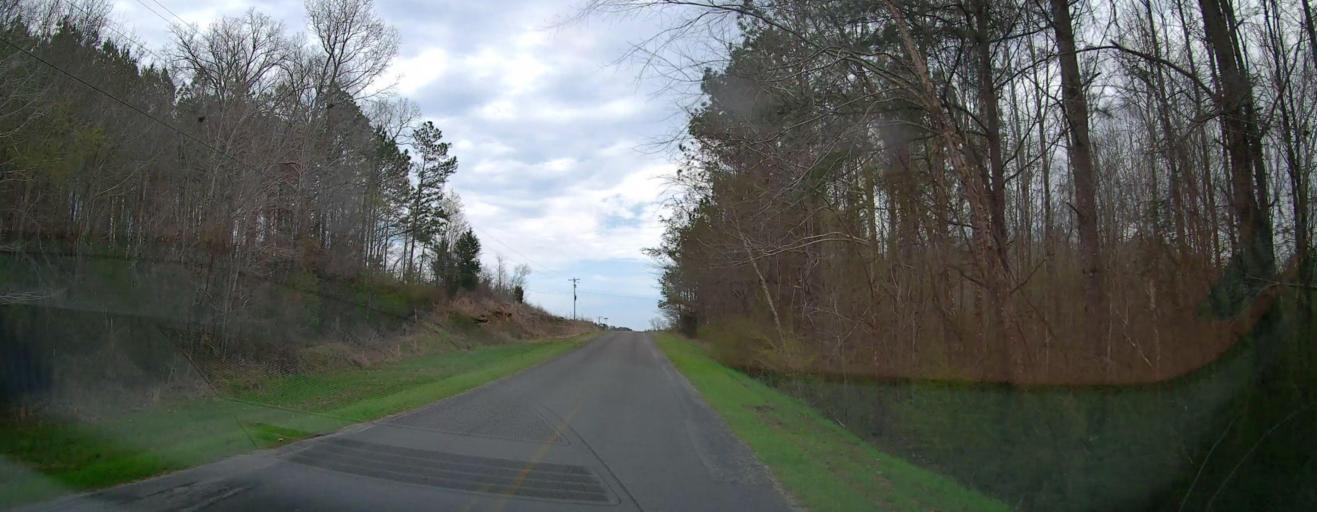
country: US
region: Alabama
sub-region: Marion County
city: Hamilton
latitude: 34.1973
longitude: -88.1640
